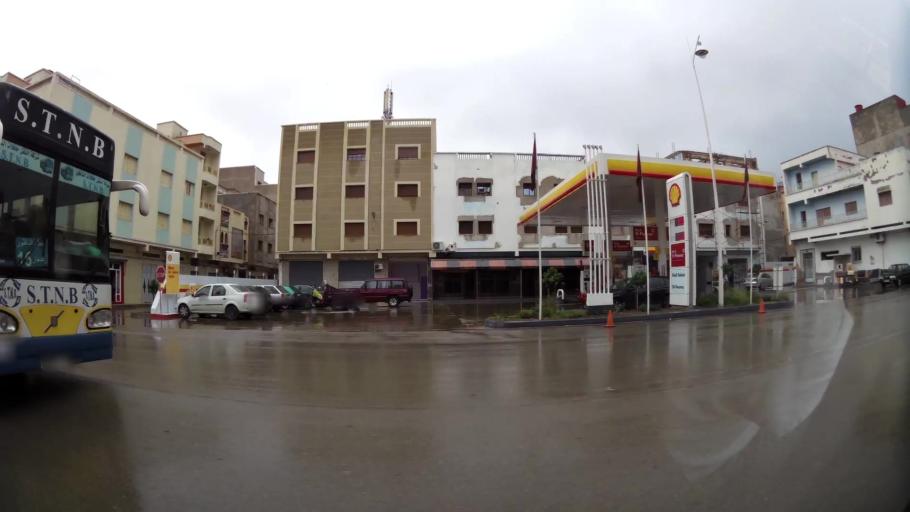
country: MA
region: Oriental
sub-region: Nador
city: Nador
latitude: 35.1544
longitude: -2.9832
